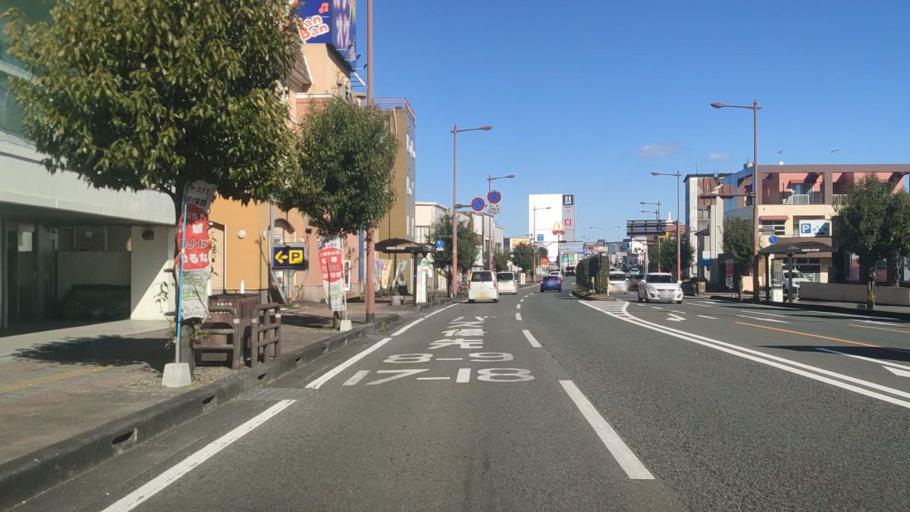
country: JP
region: Miyazaki
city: Miyakonojo
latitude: 31.7272
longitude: 131.0651
